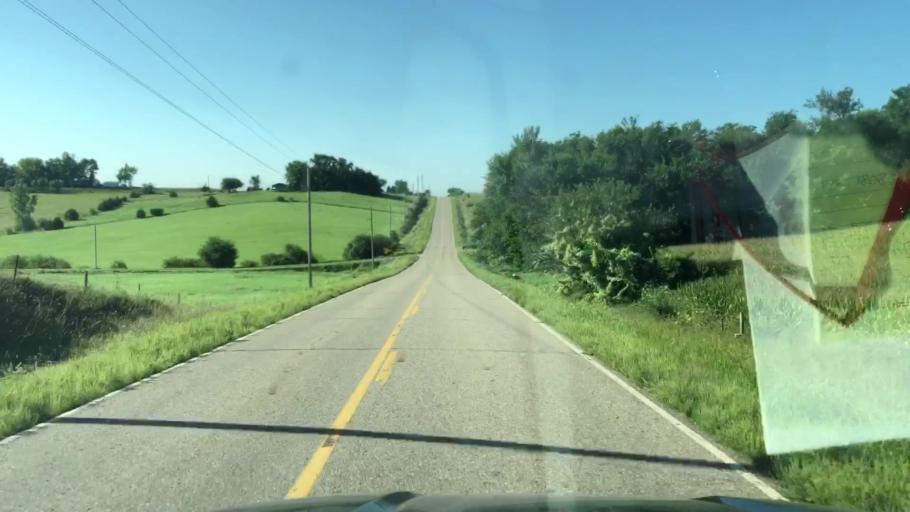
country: US
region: Iowa
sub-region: Woodbury County
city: Sergeant Bluff
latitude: 42.4350
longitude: -96.2136
